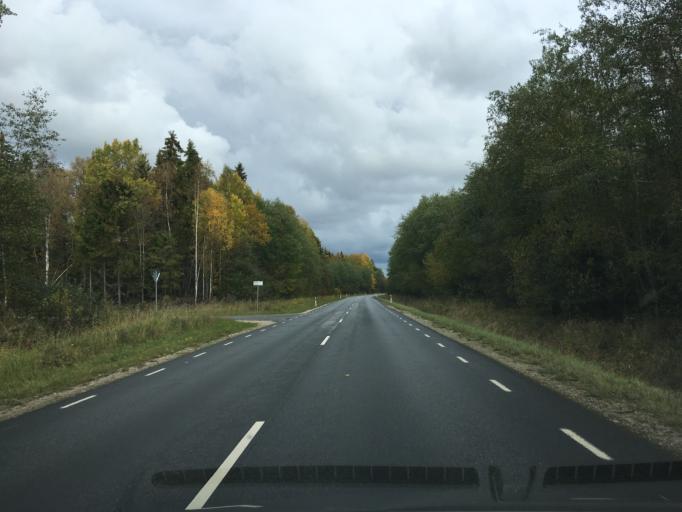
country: EE
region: Harju
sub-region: Anija vald
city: Kehra
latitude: 59.2702
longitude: 25.3560
